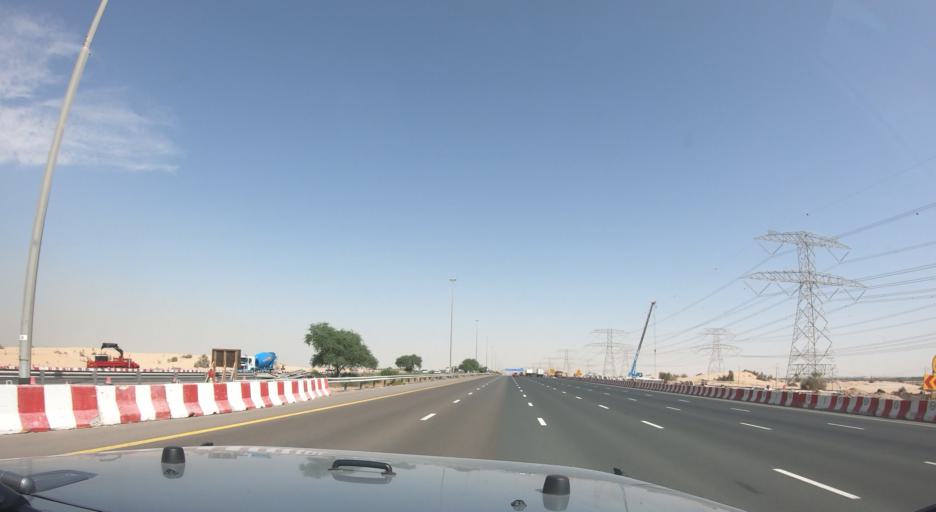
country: AE
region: Ash Shariqah
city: Sharjah
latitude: 25.1793
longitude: 55.5174
